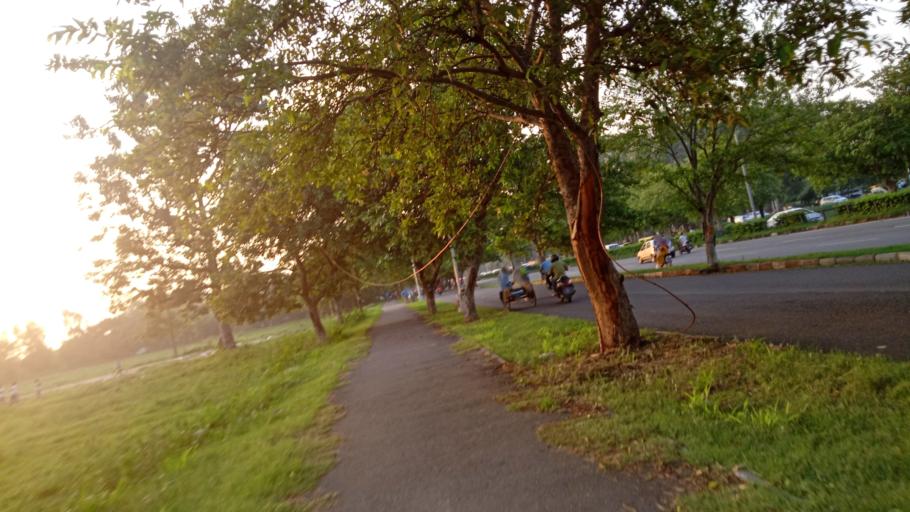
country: IN
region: Chandigarh
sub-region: Chandigarh
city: Chandigarh
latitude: 30.7492
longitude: 76.7503
